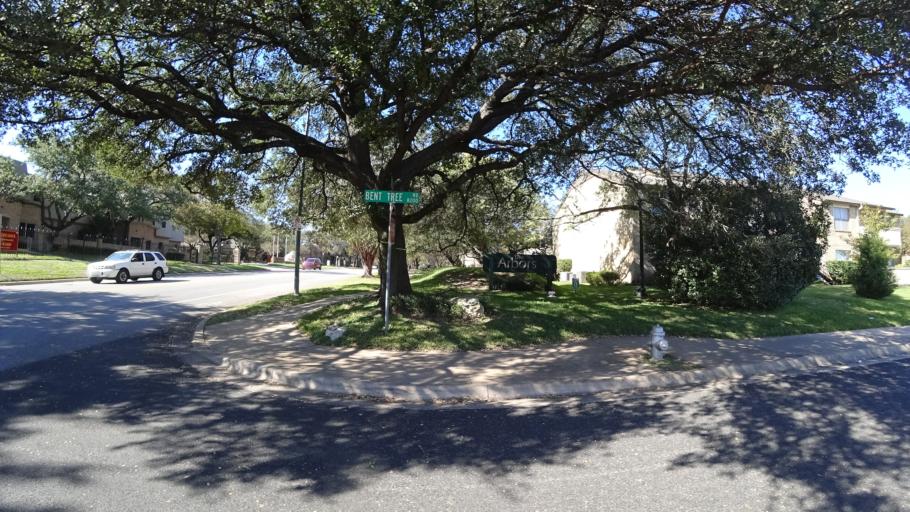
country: US
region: Texas
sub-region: Williamson County
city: Jollyville
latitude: 30.3694
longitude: -97.7447
